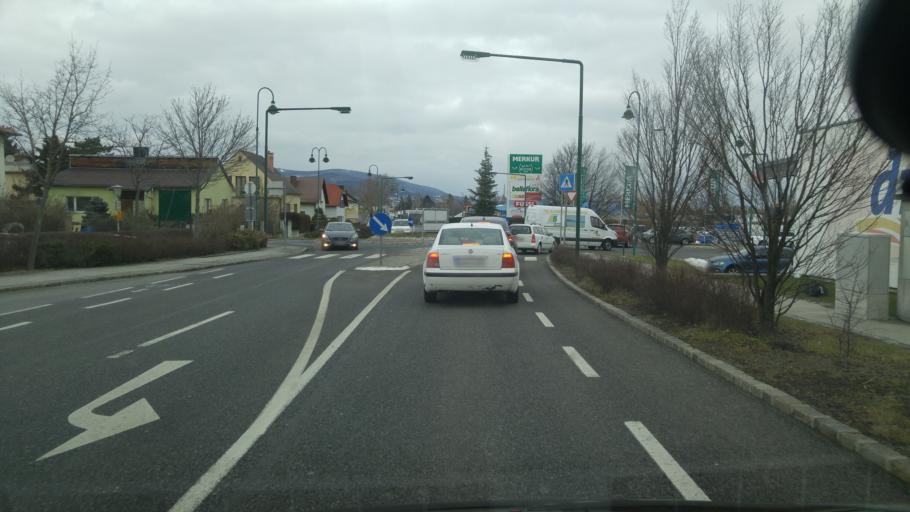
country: AT
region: Lower Austria
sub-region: Politischer Bezirk Baden
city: Bad Voslau
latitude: 47.9771
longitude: 16.2196
